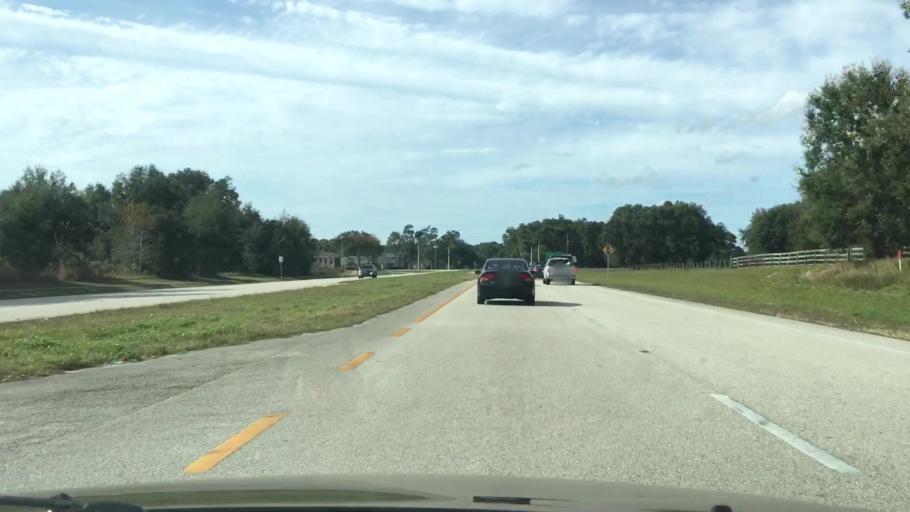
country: US
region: Florida
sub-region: Volusia County
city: North DeLand
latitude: 29.0546
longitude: -81.3214
